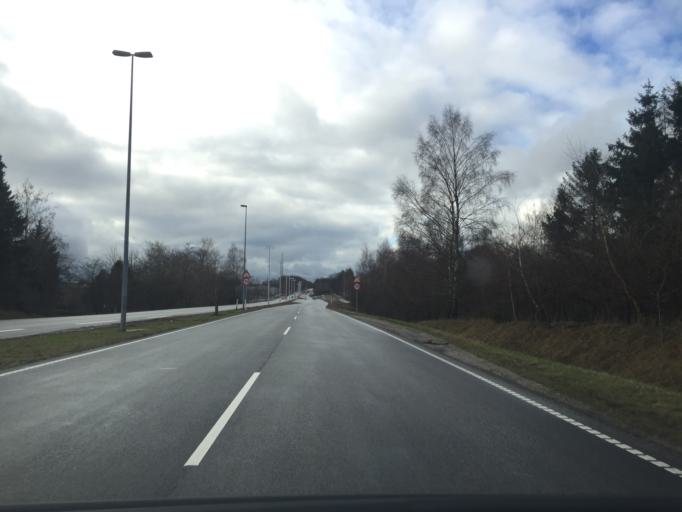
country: DK
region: Capital Region
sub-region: Fureso Kommune
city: Farum
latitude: 55.8234
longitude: 12.3729
